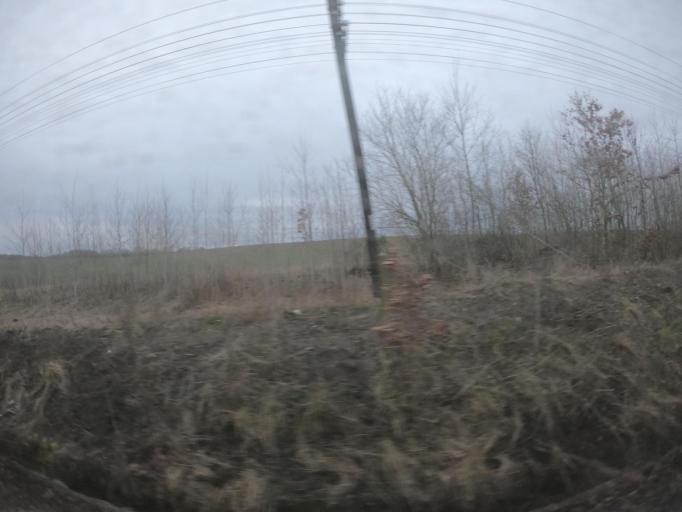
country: PL
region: West Pomeranian Voivodeship
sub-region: Powiat szczecinecki
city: Szczecinek
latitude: 53.6787
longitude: 16.6795
